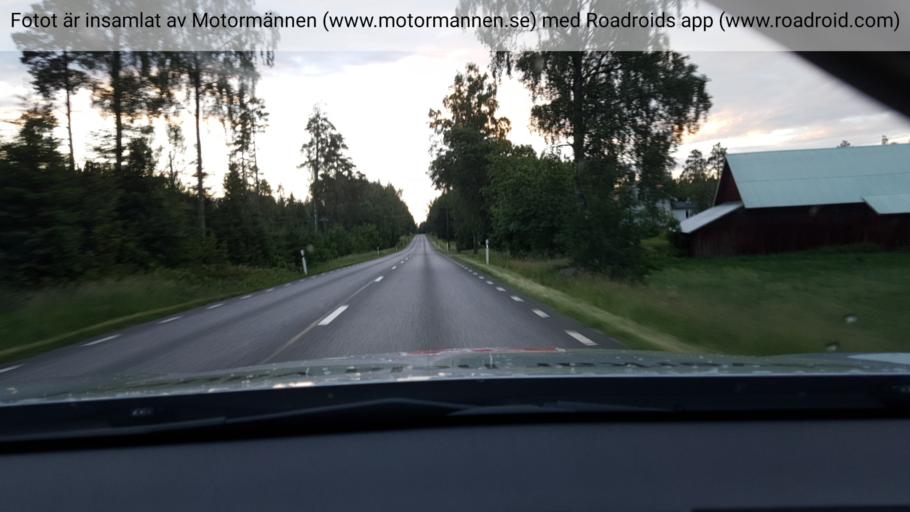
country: SE
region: Joenkoeping
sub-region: Mullsjo Kommun
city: Mullsjoe
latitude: 58.0580
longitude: 13.8055
